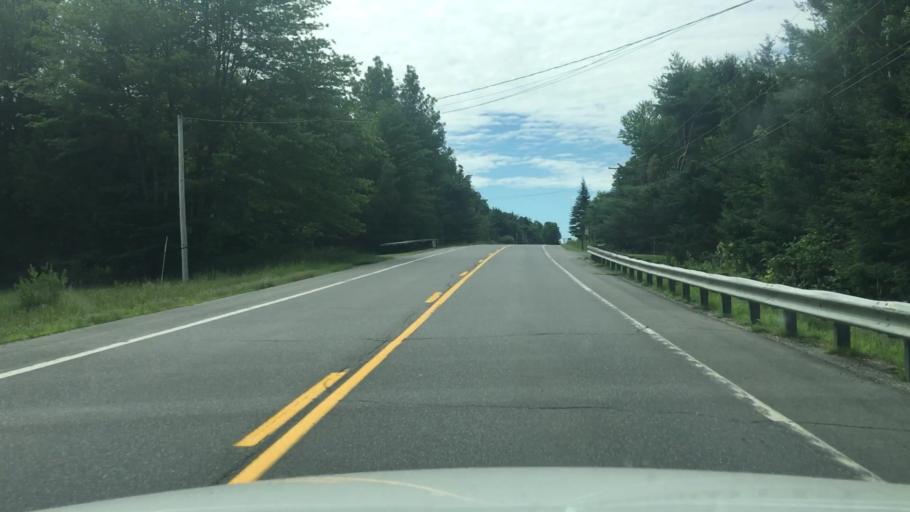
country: US
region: Maine
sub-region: Waldo County
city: Troy
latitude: 44.5909
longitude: -69.2819
